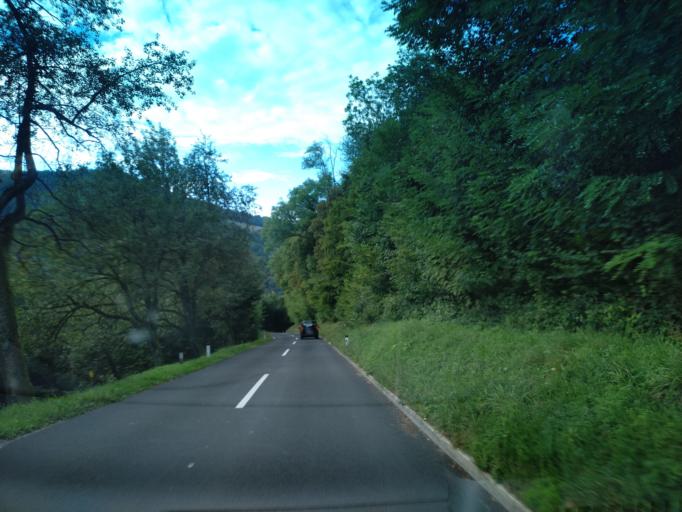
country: AT
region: Styria
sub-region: Politischer Bezirk Leibnitz
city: Leibnitz
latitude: 46.7850
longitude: 15.5236
